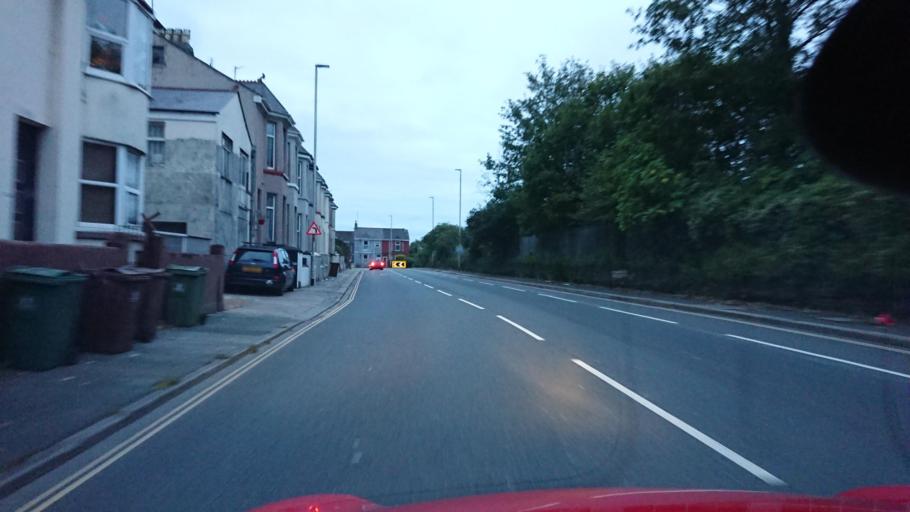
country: GB
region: England
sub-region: Cornwall
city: Torpoint
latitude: 50.3985
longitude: -4.1834
